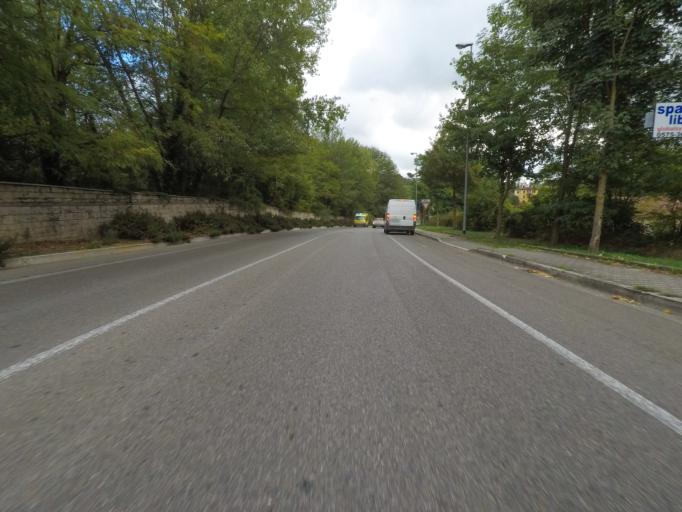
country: IT
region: Tuscany
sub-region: Provincia di Siena
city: Siena
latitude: 43.3281
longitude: 11.3361
